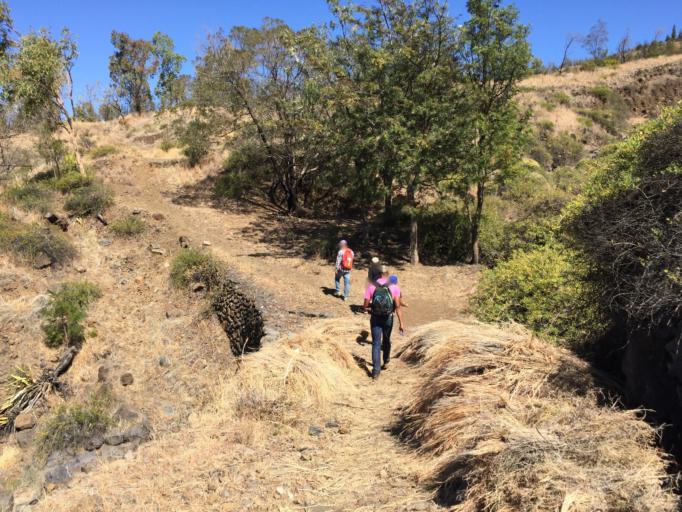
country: CV
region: Mosteiros
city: Porto dos Mosteiros
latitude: 15.0080
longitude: -24.3651
